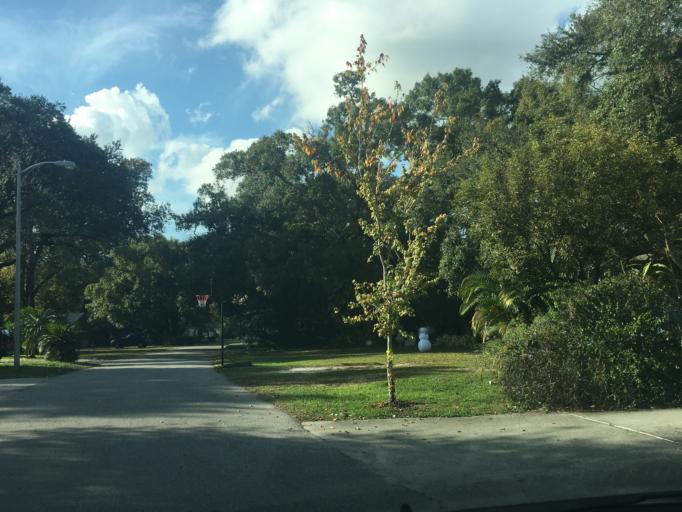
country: US
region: Florida
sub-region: Hillsborough County
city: Egypt Lake-Leto
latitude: 27.9935
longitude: -82.4686
